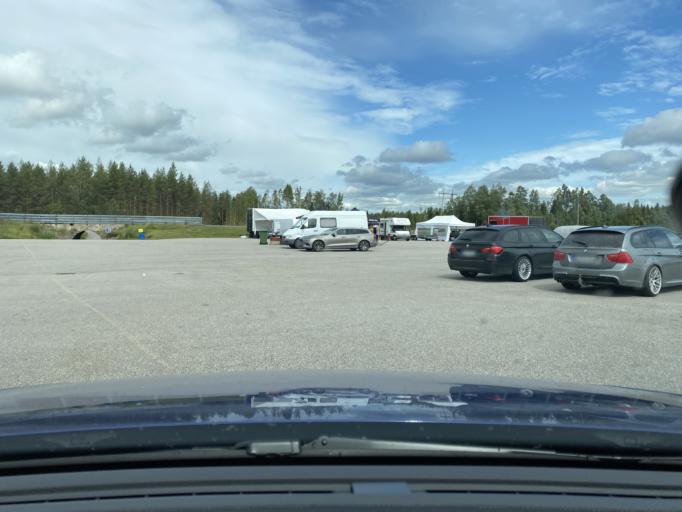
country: FI
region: Southern Ostrobothnia
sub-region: Seinaejoki
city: Jurva
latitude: 62.6257
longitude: 22.0178
